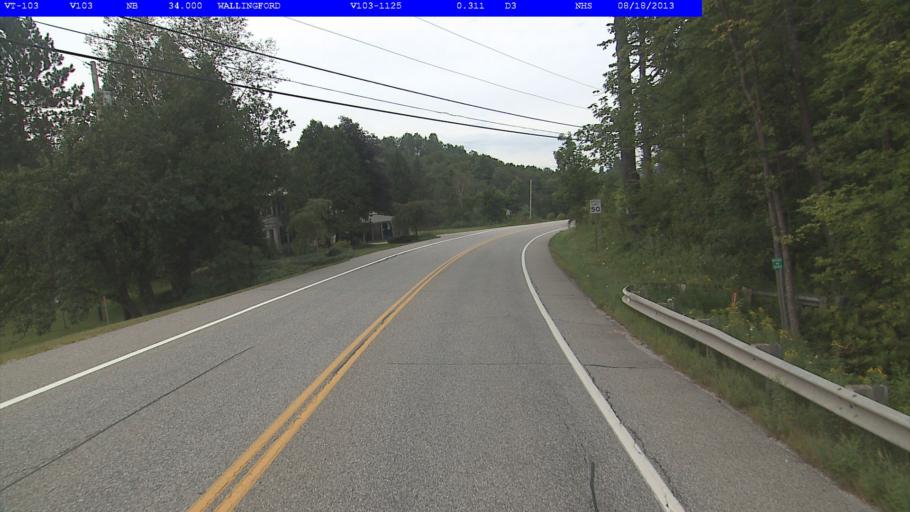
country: US
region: Vermont
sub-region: Rutland County
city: Rutland
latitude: 43.4513
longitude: -72.8778
